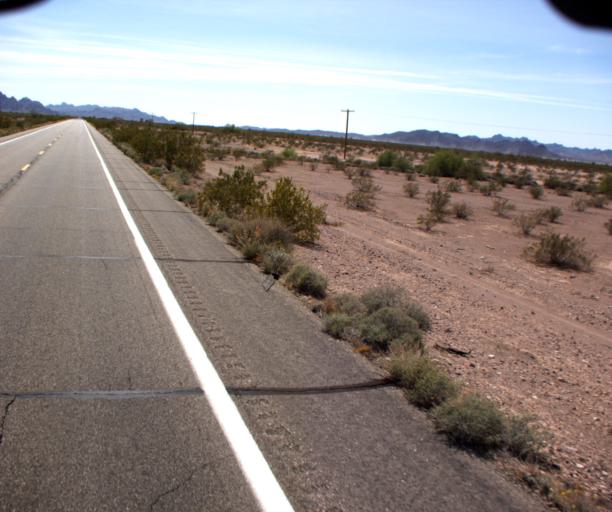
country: US
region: Arizona
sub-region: La Paz County
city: Quartzsite
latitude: 33.3678
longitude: -114.2171
